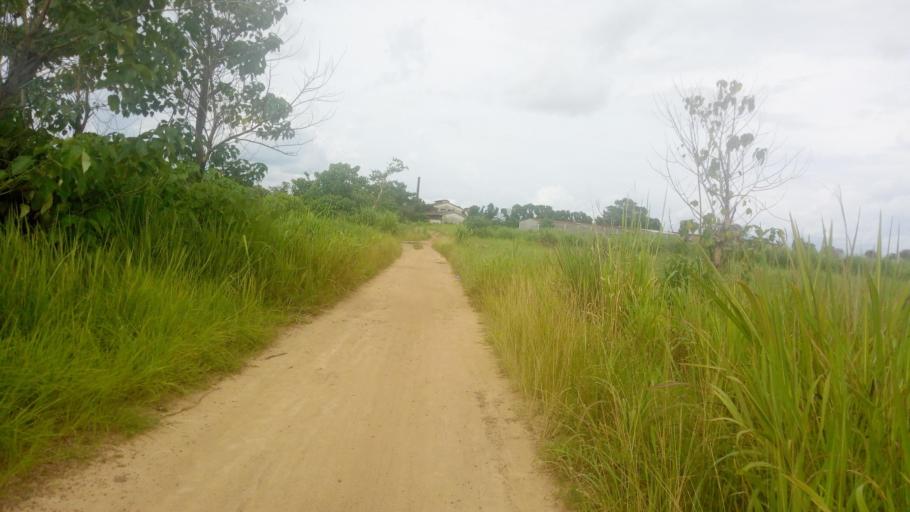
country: SL
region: Northern Province
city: Magburaka
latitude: 8.6732
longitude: -12.0218
